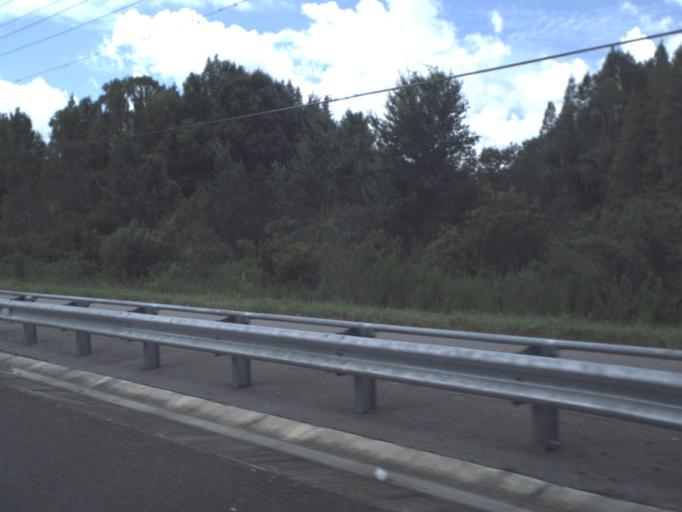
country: US
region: Florida
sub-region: Pasco County
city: Wesley Chapel
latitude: 28.2156
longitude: -82.3535
